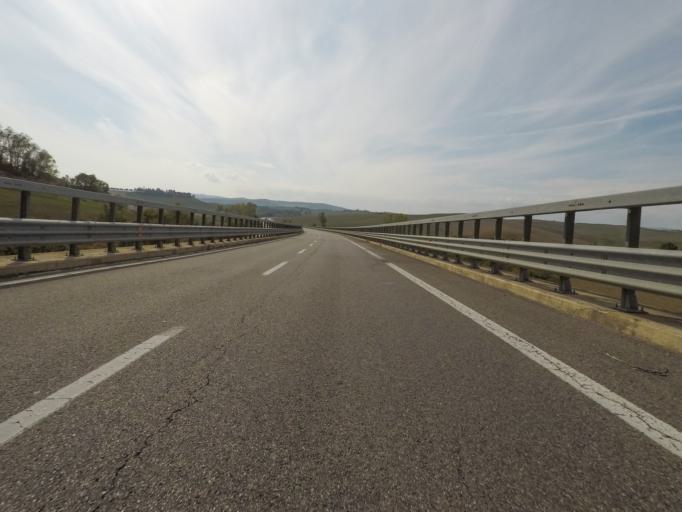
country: IT
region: Tuscany
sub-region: Provincia di Siena
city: Isola D'Arbia
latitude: 43.2677
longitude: 11.3297
